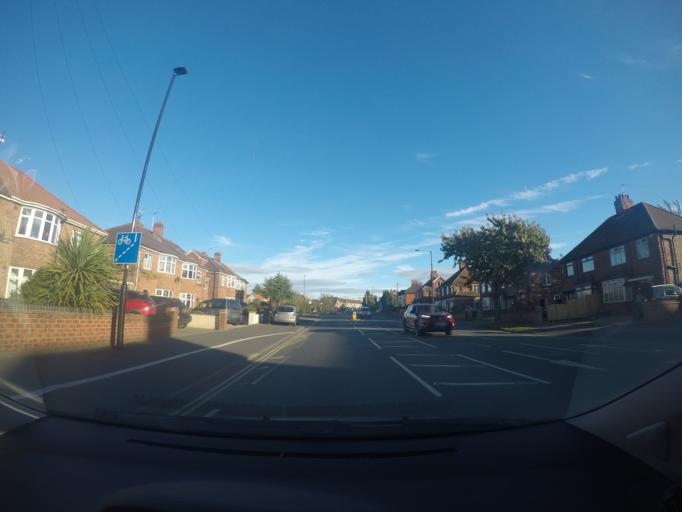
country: GB
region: England
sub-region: City of York
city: Skelton
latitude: 53.9643
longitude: -1.1205
